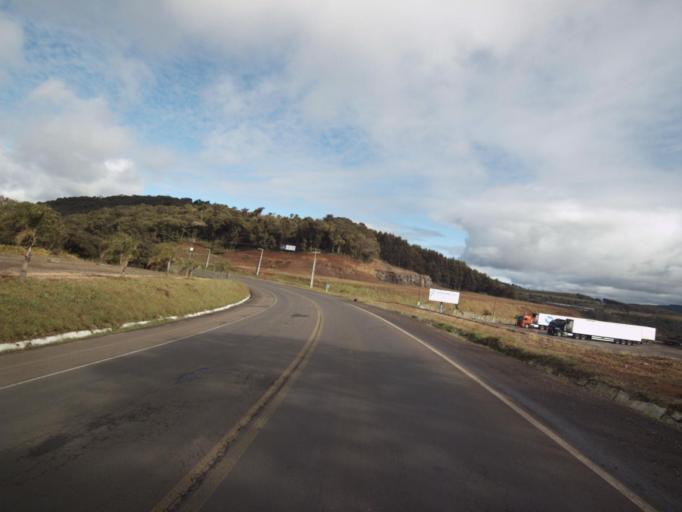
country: BR
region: Santa Catarina
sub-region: Concordia
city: Concordia
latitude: -27.2029
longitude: -51.9475
